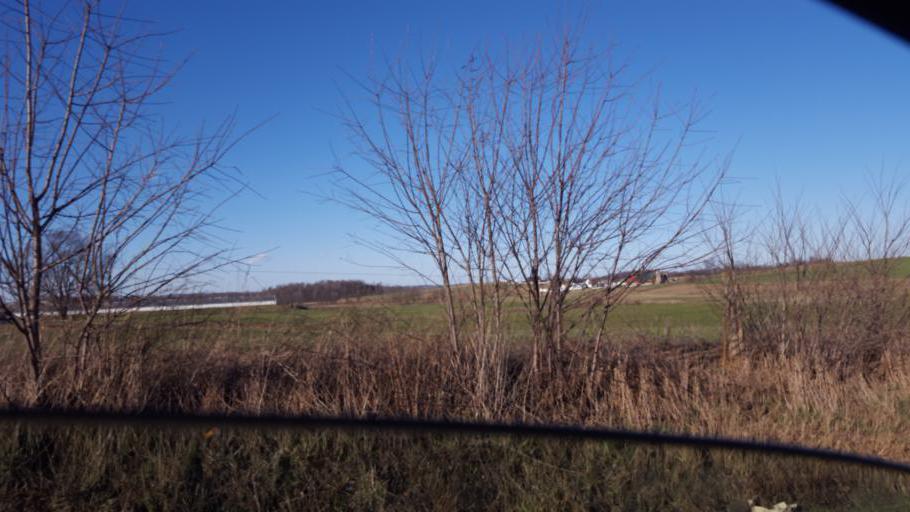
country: US
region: Ohio
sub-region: Holmes County
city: Millersburg
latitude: 40.5863
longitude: -81.7735
